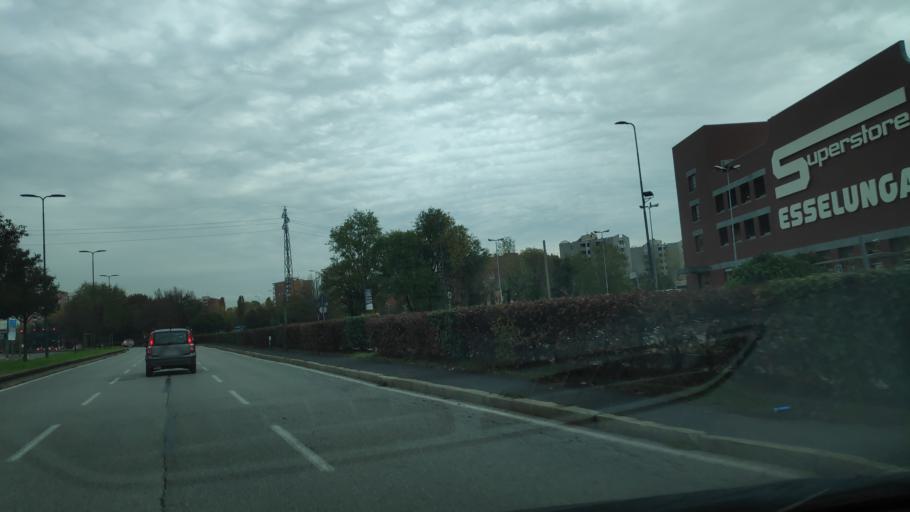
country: IT
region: Lombardy
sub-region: Citta metropolitana di Milano
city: Rozzano
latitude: 45.4208
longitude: 9.1765
